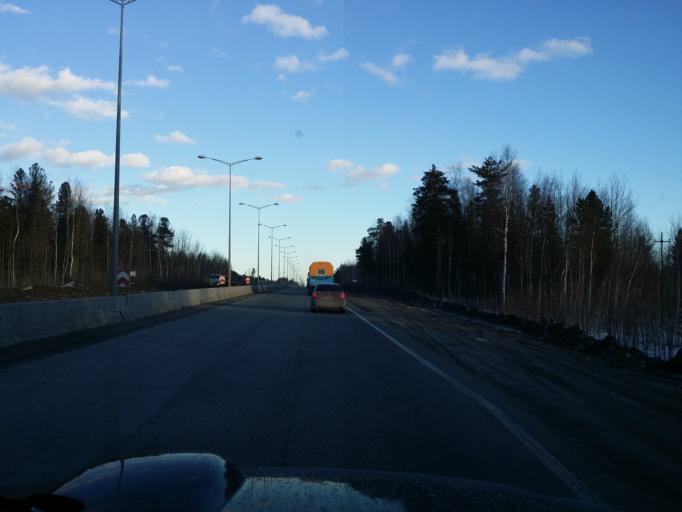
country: RU
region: Khanty-Mansiyskiy Avtonomnyy Okrug
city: Nizhnevartovsk
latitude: 61.0111
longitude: 76.4007
